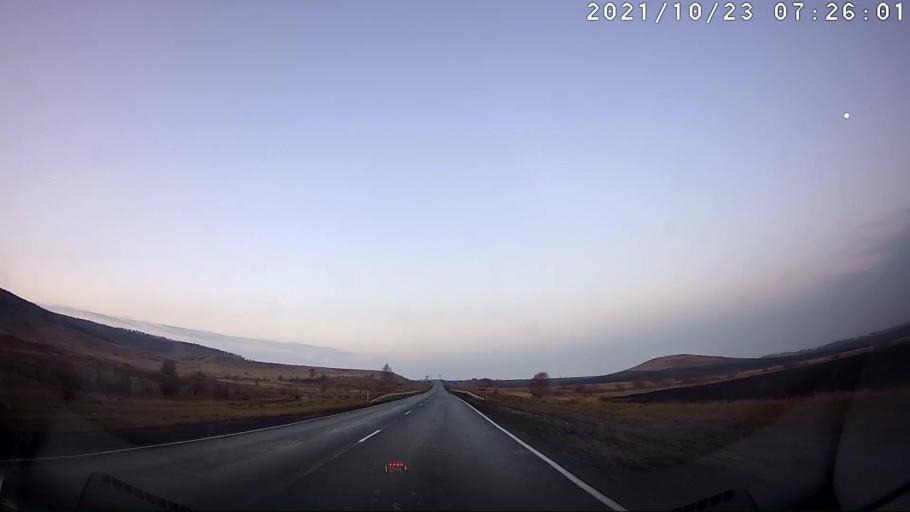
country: RU
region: Saratov
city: Alekseyevka
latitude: 52.3530
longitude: 47.9428
